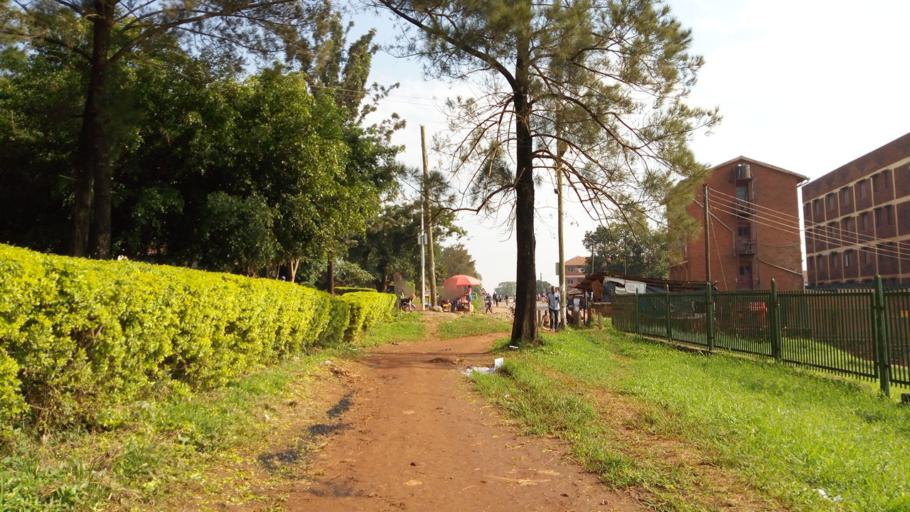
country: UG
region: Central Region
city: Kampala Central Division
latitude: 0.3377
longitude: 32.5702
